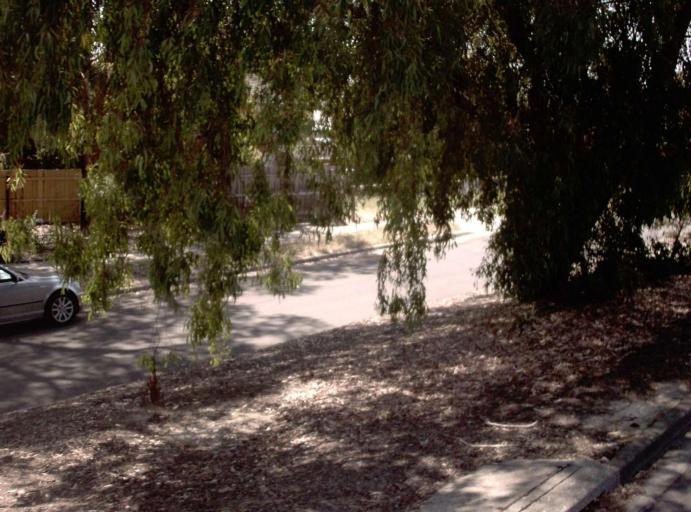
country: AU
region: Victoria
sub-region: Whitehorse
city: Forest Hill
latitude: -37.8385
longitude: 145.1718
